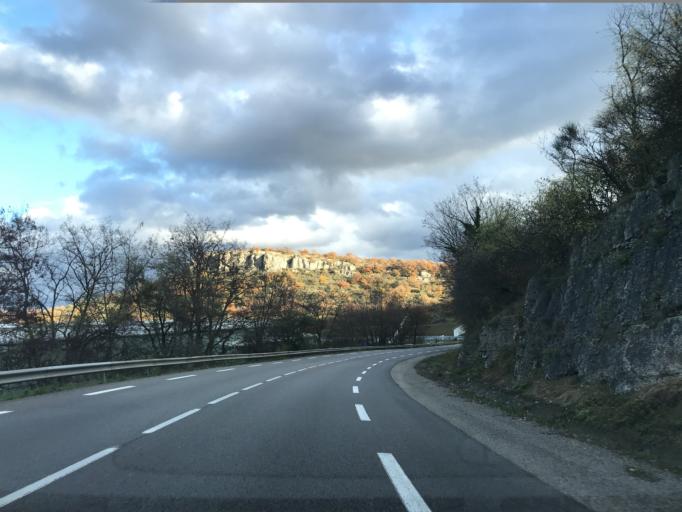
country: FR
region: Rhone-Alpes
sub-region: Departement de l'Ardeche
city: Alissas
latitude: 44.7112
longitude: 4.6209
